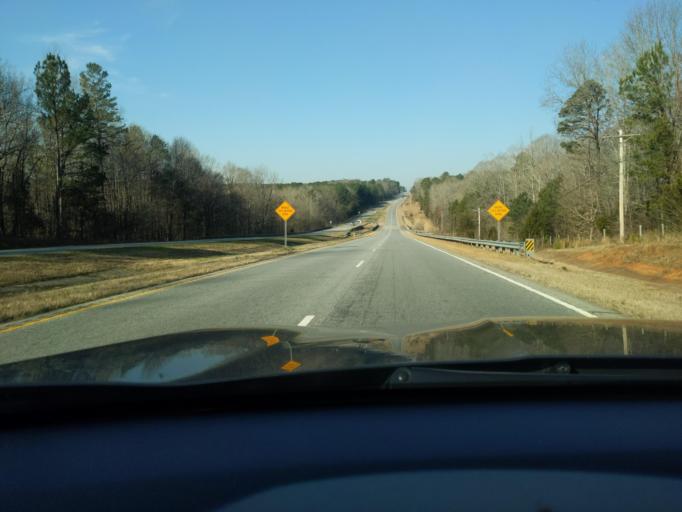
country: US
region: South Carolina
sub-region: Abbeville County
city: Abbeville
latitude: 34.1846
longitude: -82.3250
